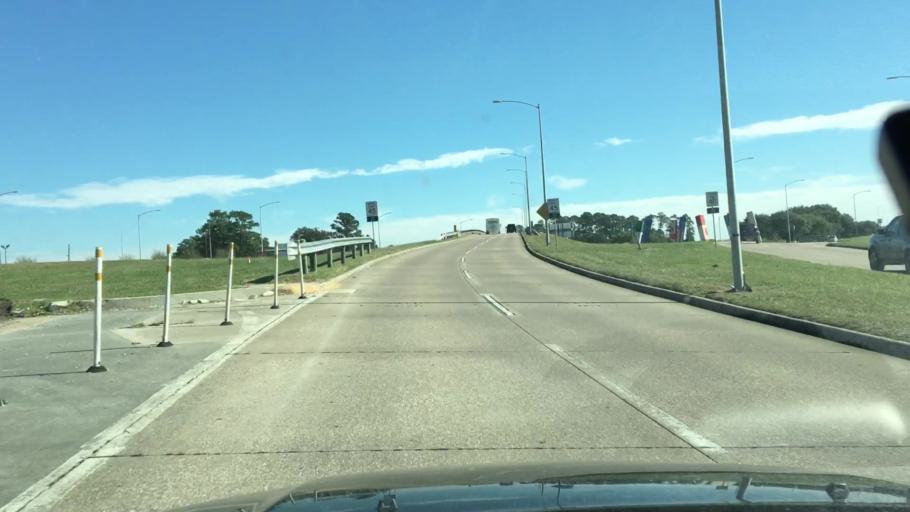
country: US
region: Texas
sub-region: Harris County
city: Humble
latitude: 29.9859
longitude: -95.3292
